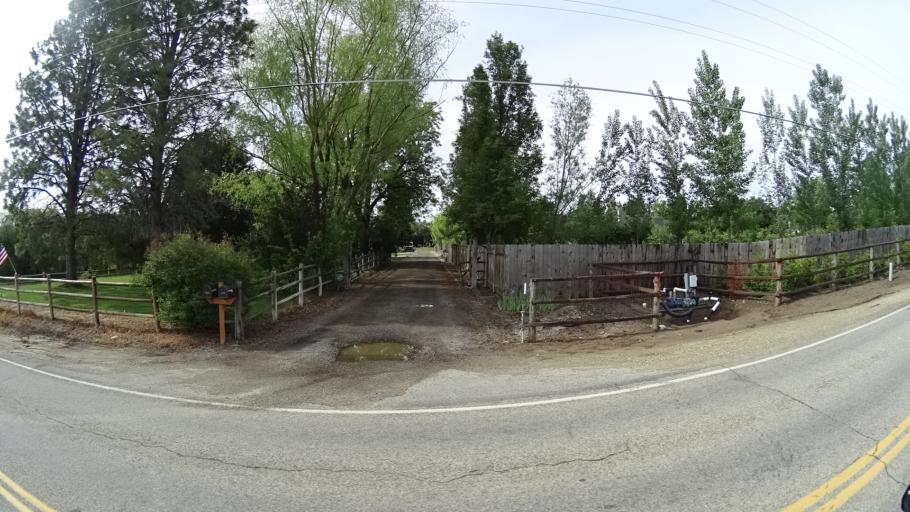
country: US
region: Idaho
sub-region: Ada County
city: Eagle
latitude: 43.7208
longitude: -116.3752
